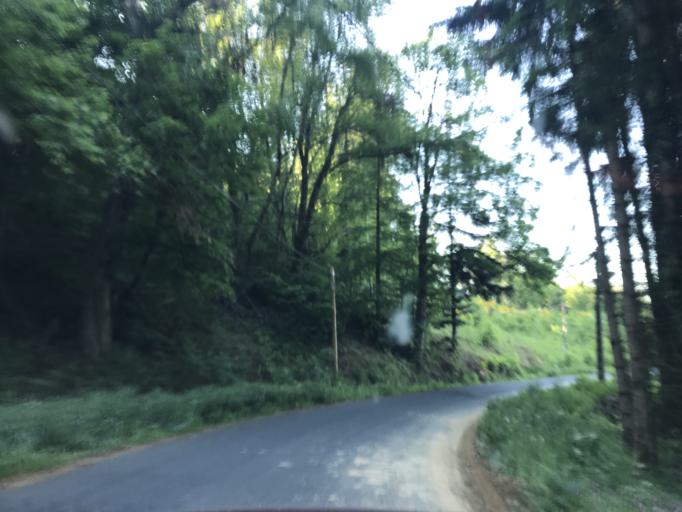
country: FR
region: Auvergne
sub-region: Departement du Puy-de-Dome
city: Job
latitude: 45.6918
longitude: 3.6857
